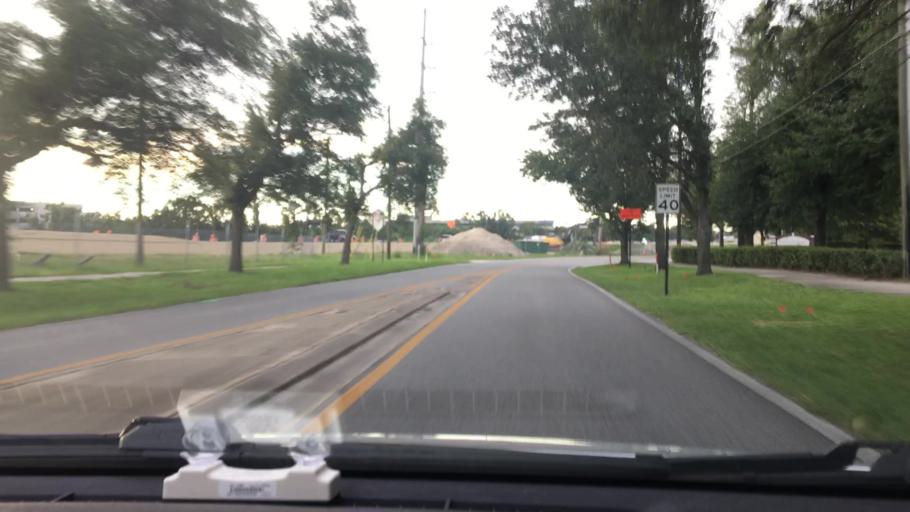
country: US
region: Florida
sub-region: Orange County
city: Eatonville
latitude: 28.6336
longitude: -81.3858
